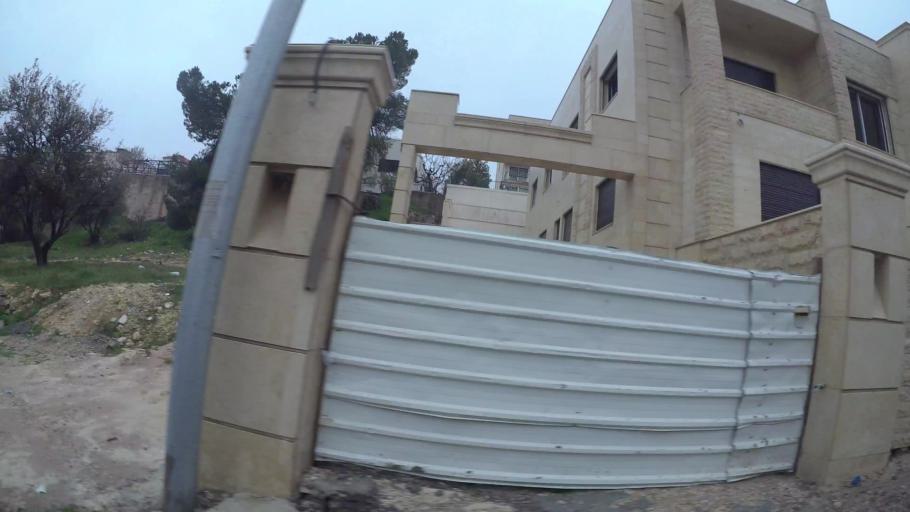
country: JO
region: Amman
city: Al Jubayhah
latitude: 32.0095
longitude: 35.8348
